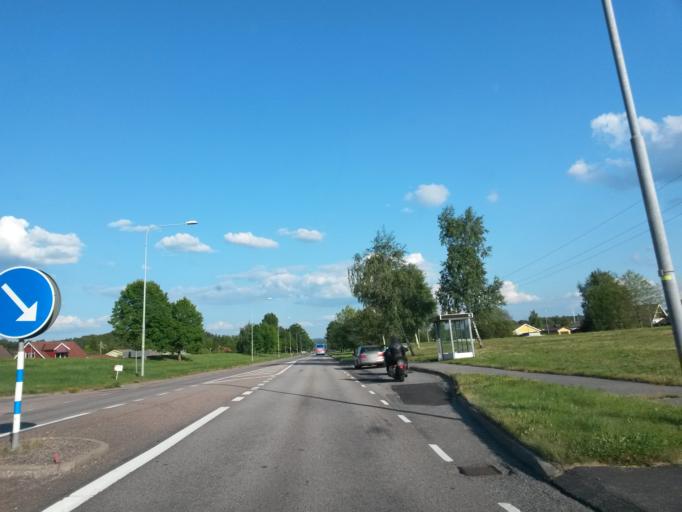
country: SE
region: Vaestra Goetaland
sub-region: Alingsas Kommun
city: Alingsas
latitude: 57.9472
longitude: 12.5053
